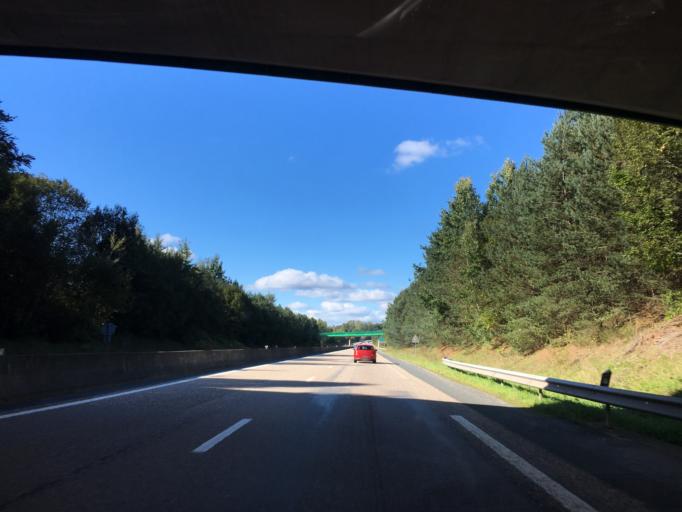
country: FR
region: Lorraine
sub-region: Departement de Meurthe-et-Moselle
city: Baccarat
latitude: 48.4409
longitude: 6.7623
